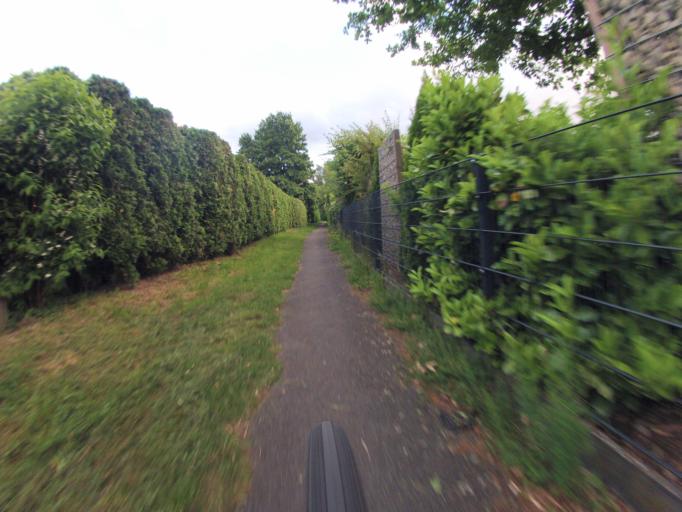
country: DE
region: North Rhine-Westphalia
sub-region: Regierungsbezirk Munster
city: Birgte
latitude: 52.2921
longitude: 7.6470
